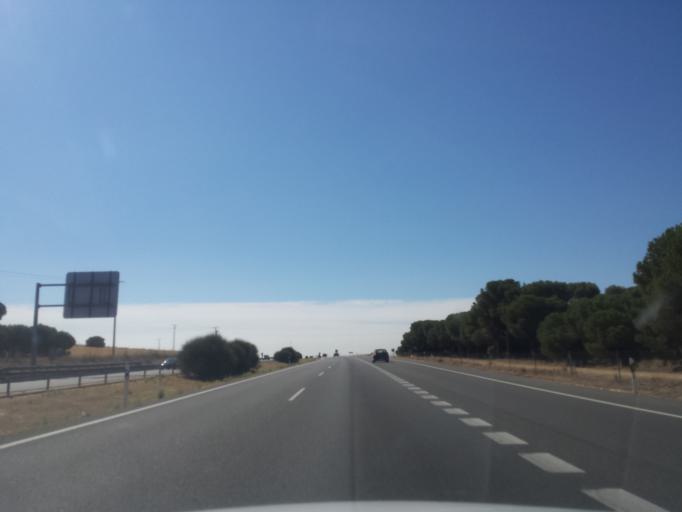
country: ES
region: Castille and Leon
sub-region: Provincia de Valladolid
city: Bercero
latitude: 41.5400
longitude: -5.0679
